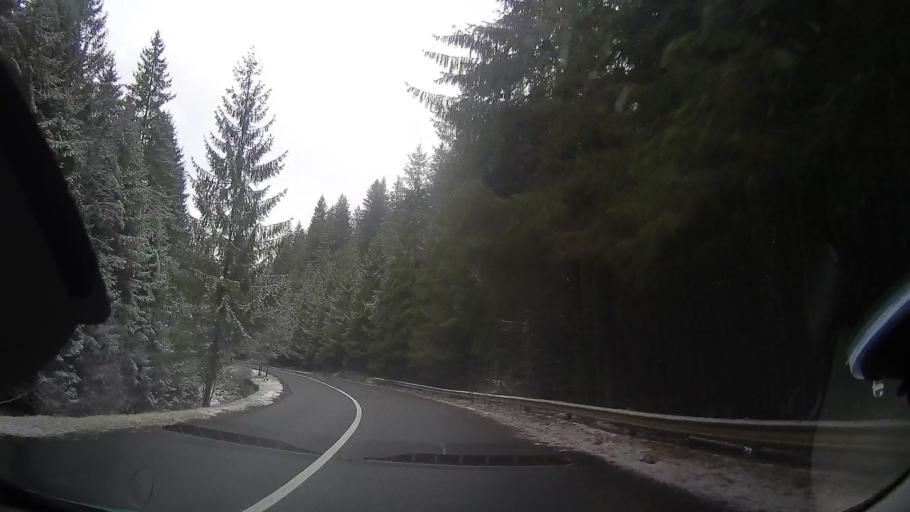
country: RO
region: Cluj
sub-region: Comuna Calatele
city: Calatele
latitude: 46.7354
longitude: 23.0390
